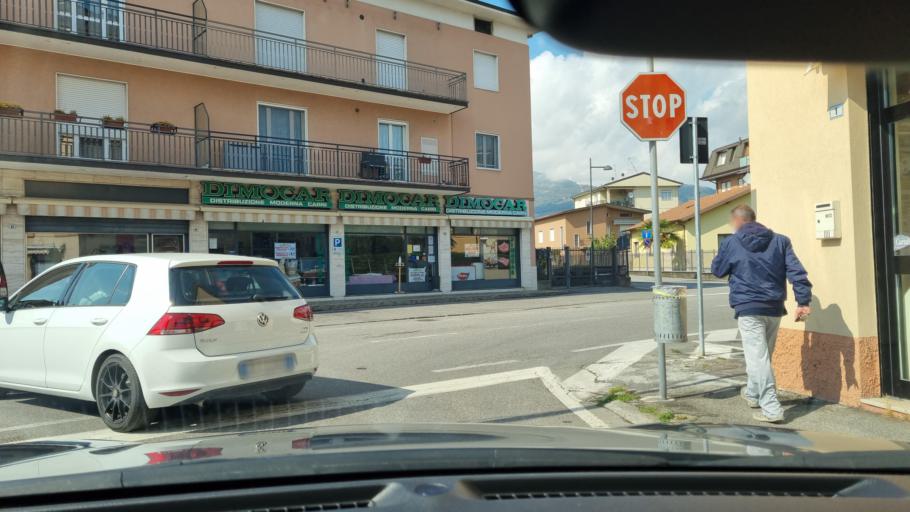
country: IT
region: Lombardy
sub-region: Provincia di Bergamo
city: Ambivere
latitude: 45.7203
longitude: 9.5491
